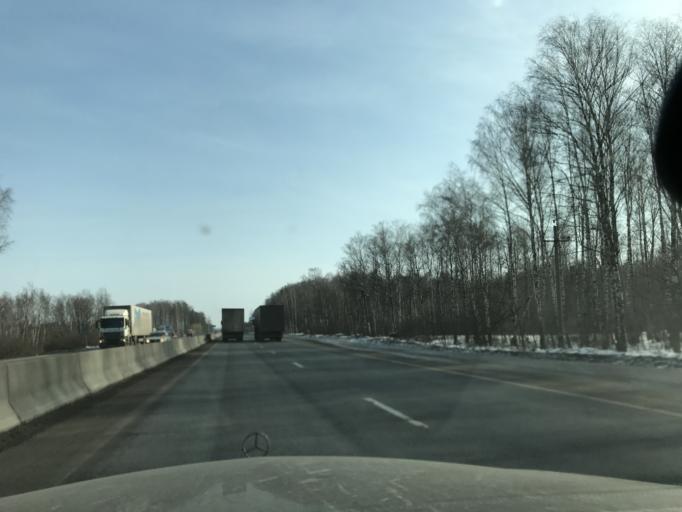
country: RU
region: Nizjnij Novgorod
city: Gorbatovka
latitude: 56.3080
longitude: 43.7235
